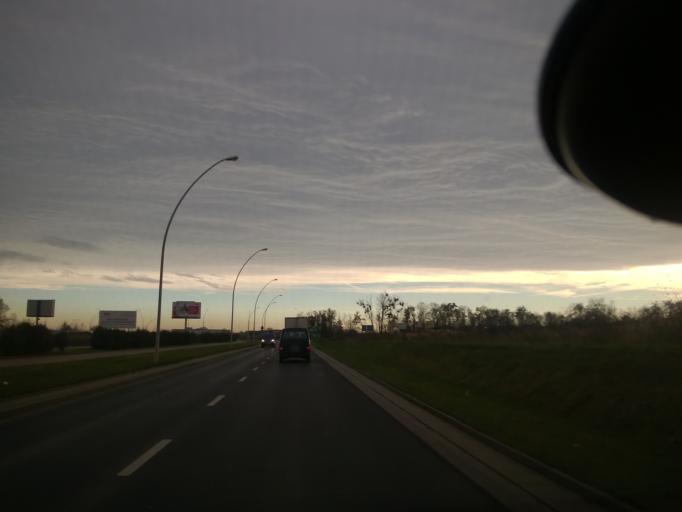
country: PL
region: Lower Silesian Voivodeship
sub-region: Powiat wroclawski
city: Bielany Wroclawskie
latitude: 51.0532
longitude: 16.9626
